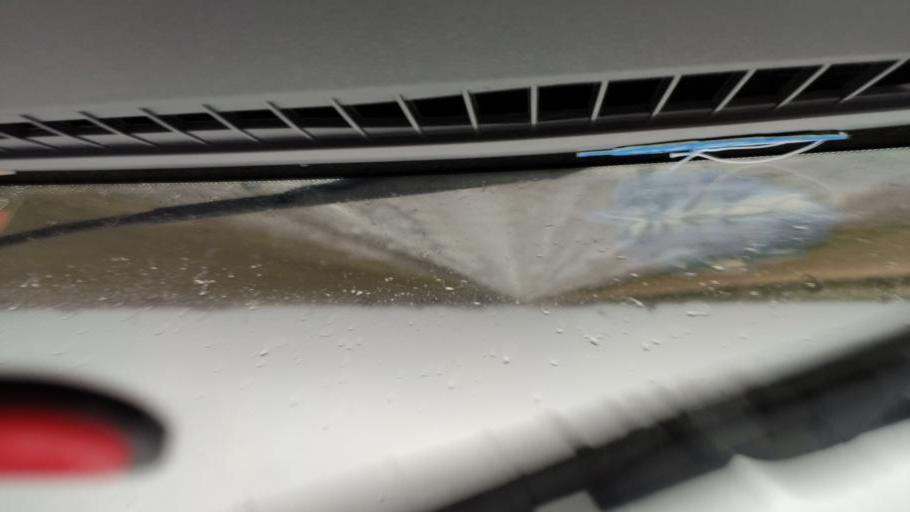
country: RU
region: Tatarstan
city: Cheremshan
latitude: 54.7291
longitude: 51.3188
